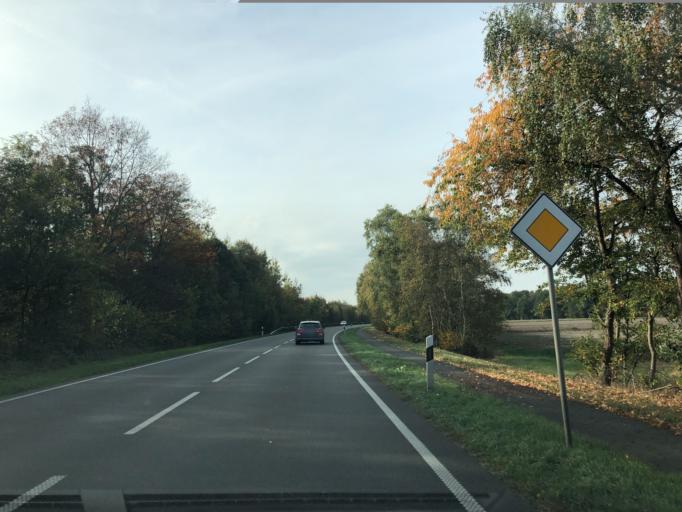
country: DE
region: Lower Saxony
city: Hilkenbrook
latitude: 53.0253
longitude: 7.7359
